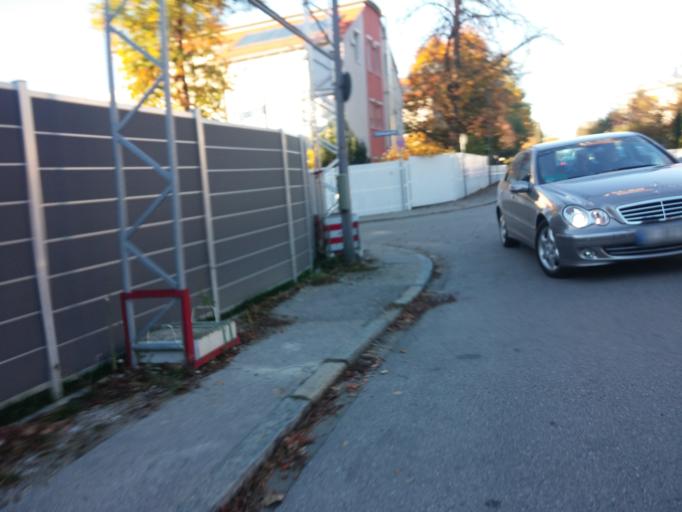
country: DE
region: Bavaria
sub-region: Upper Bavaria
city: Haar
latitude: 48.1104
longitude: 11.7089
